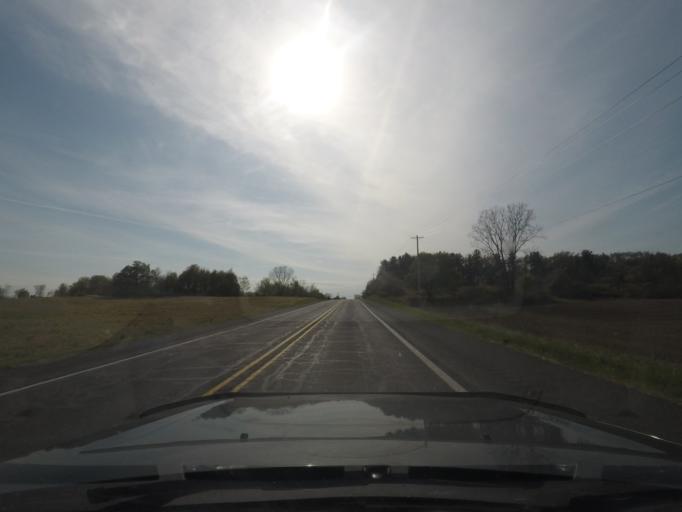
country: US
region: Indiana
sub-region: LaPorte County
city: Hudson Lake
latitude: 41.7982
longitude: -86.5087
